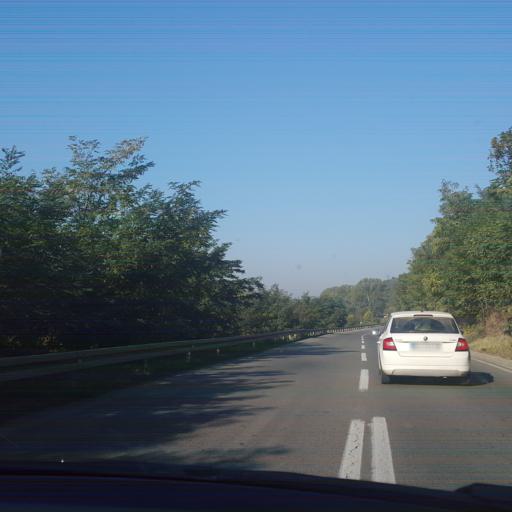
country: RS
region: Central Serbia
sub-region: Toplicki Okrug
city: Prokuplje
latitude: 43.2327
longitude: 21.5442
